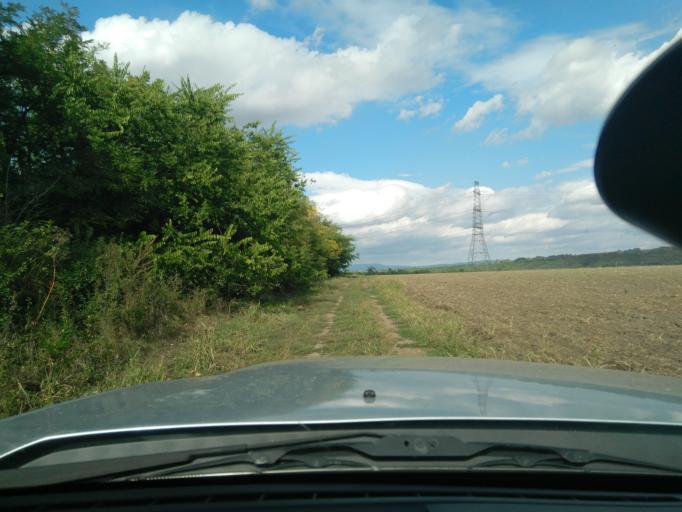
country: HU
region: Fejer
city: Bicske
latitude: 47.4591
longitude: 18.6614
